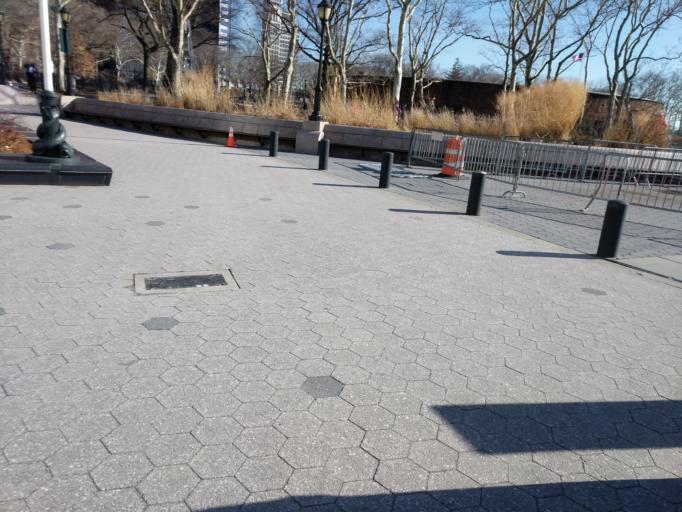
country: US
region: New York
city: New York City
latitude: 40.7042
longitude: -74.0176
